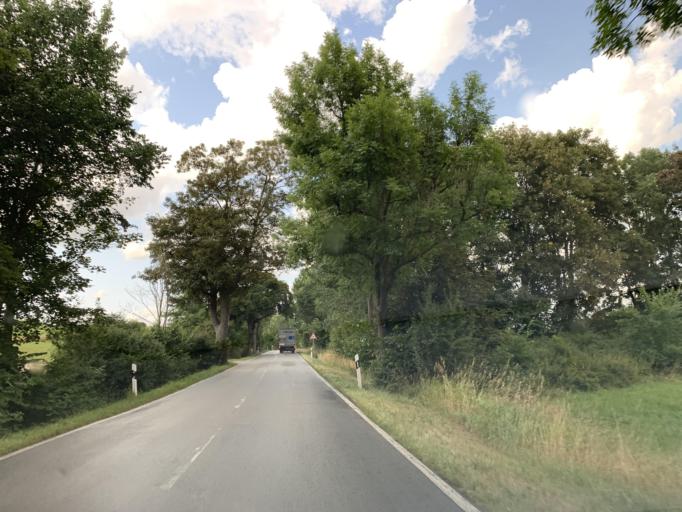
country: DE
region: Mecklenburg-Vorpommern
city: Neverin
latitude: 53.5995
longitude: 13.3295
